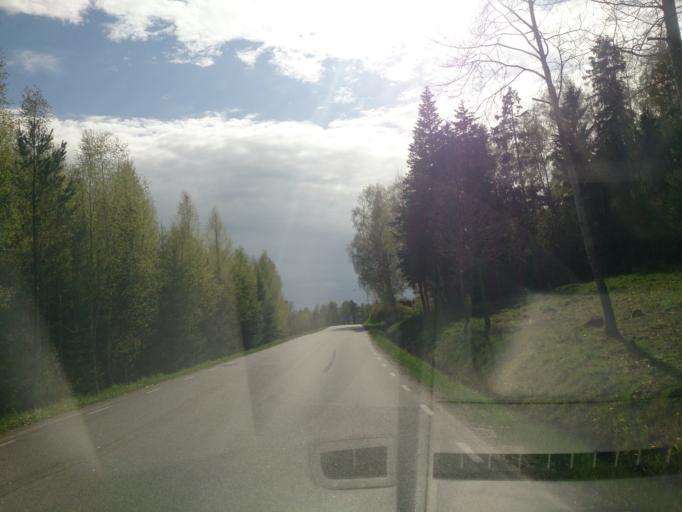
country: SE
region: OEstergoetland
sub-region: Linkopings Kommun
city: Ljungsbro
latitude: 58.5203
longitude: 15.5231
